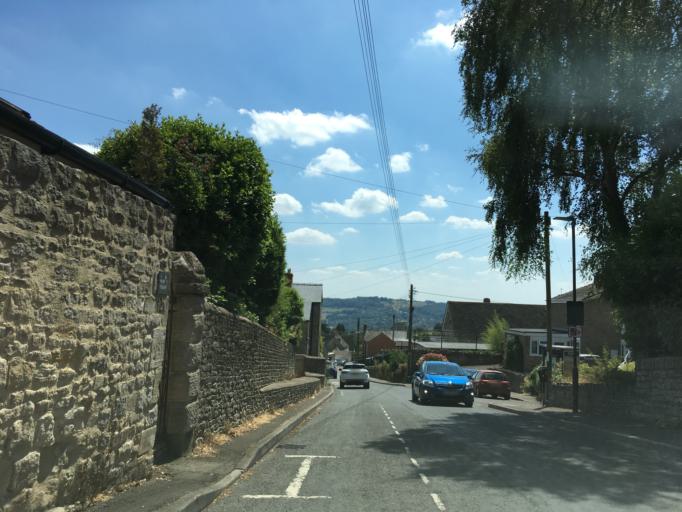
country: GB
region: England
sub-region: Gloucestershire
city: Stroud
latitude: 51.7632
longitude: -2.2338
